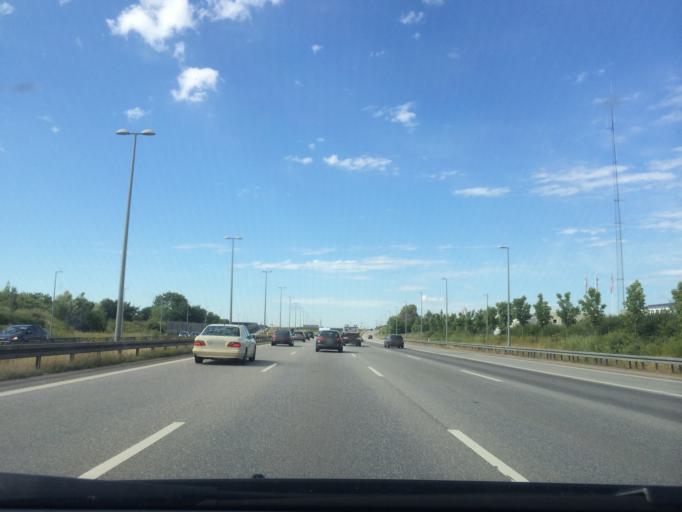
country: DK
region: Zealand
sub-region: Greve Kommune
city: Greve
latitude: 55.6055
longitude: 12.3088
